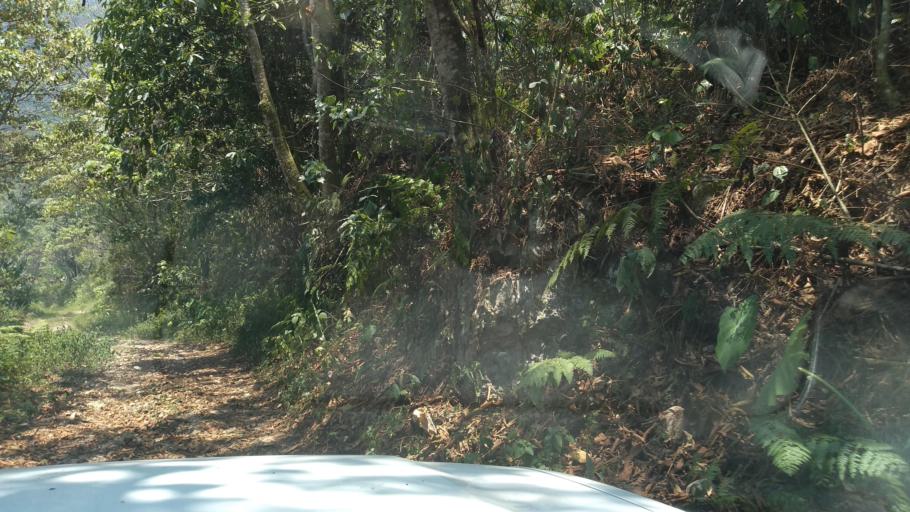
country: MX
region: Veracruz
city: Motzorongo
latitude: 18.6092
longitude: -96.7624
